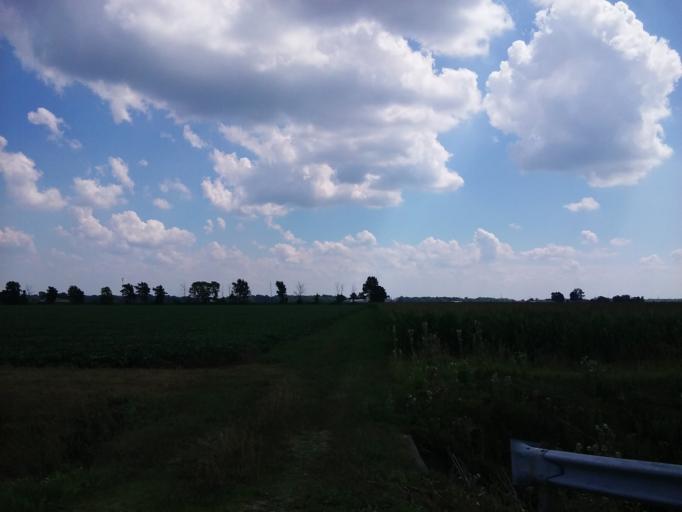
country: US
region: Ohio
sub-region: Wood County
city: Bowling Green
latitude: 41.3853
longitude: -83.5954
